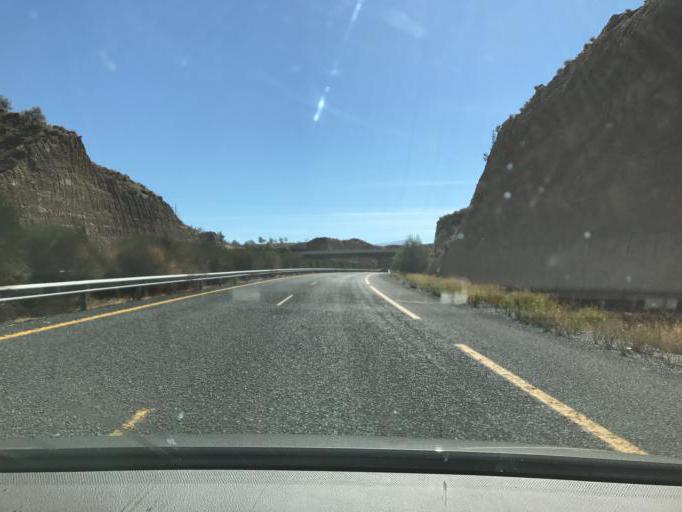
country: ES
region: Andalusia
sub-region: Provincia de Granada
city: Guadix
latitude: 37.3182
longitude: -3.1135
